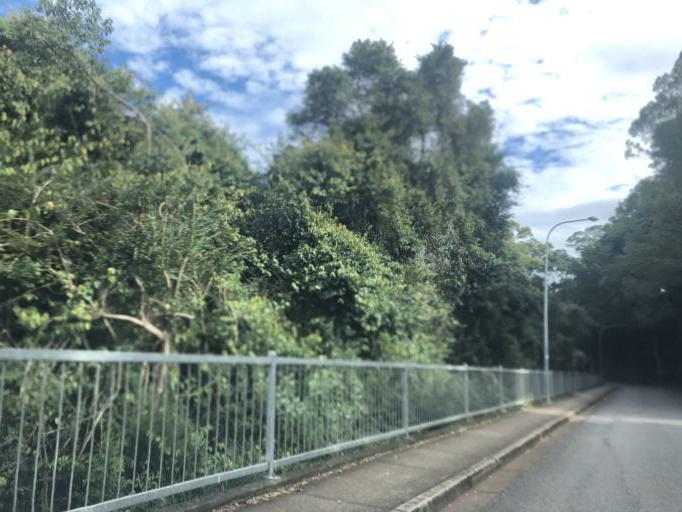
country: AU
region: New South Wales
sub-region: Bellingen
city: Bellingen
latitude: -30.4466
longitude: 152.9004
